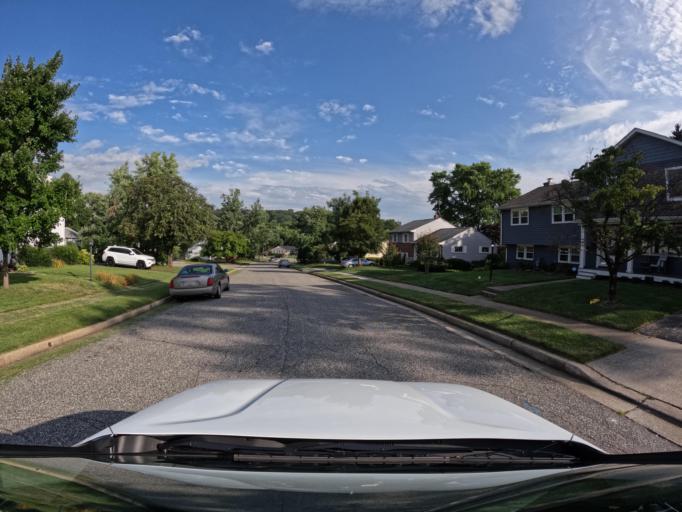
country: US
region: Maryland
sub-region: Baltimore County
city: Mays Chapel
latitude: 39.4181
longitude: -76.6443
